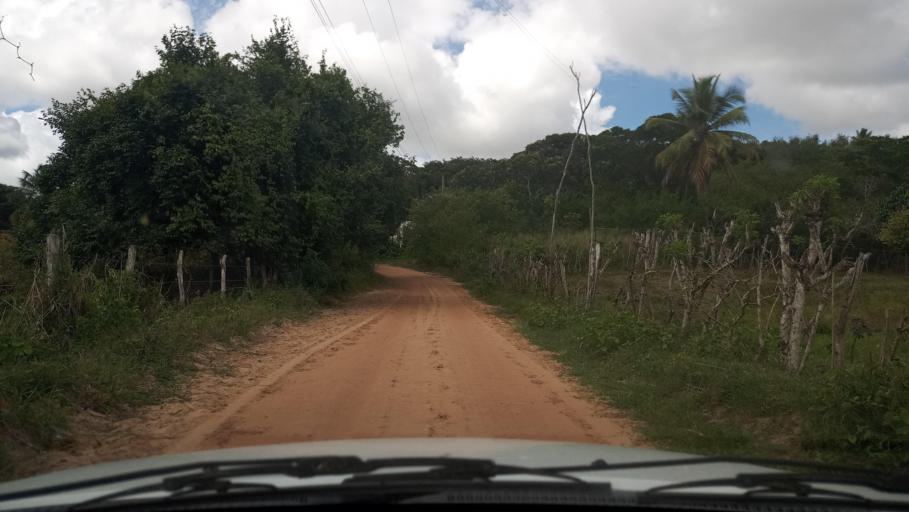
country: BR
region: Rio Grande do Norte
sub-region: Goianinha
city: Goianinha
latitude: -6.2612
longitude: -35.2530
